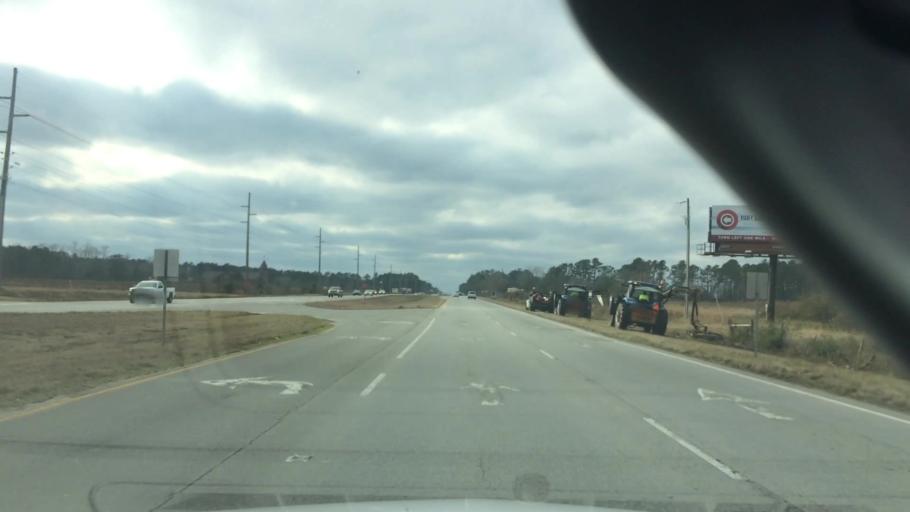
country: US
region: North Carolina
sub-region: Brunswick County
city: Shallotte
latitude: 33.9582
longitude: -78.4255
